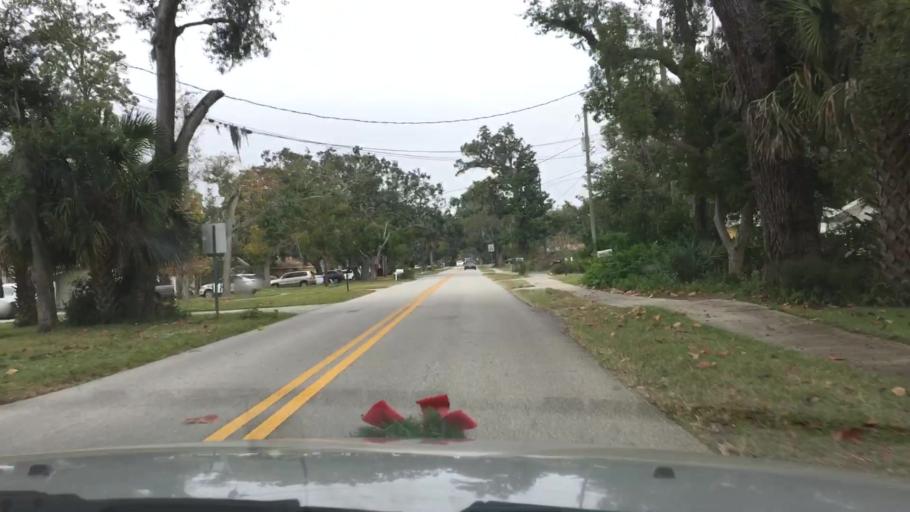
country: US
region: Florida
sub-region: Volusia County
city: Ormond Beach
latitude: 29.2950
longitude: -81.0637
